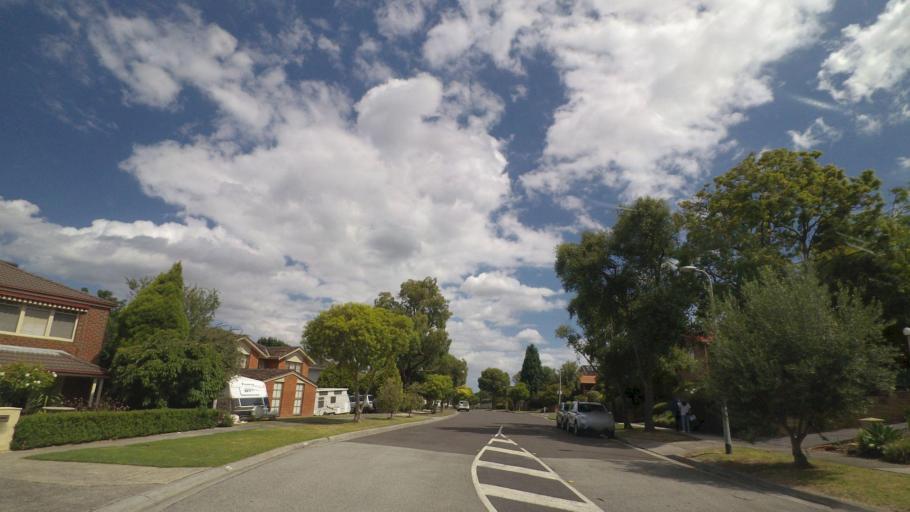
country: AU
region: Victoria
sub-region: Knox
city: Wantirna
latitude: -37.8587
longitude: 145.2229
